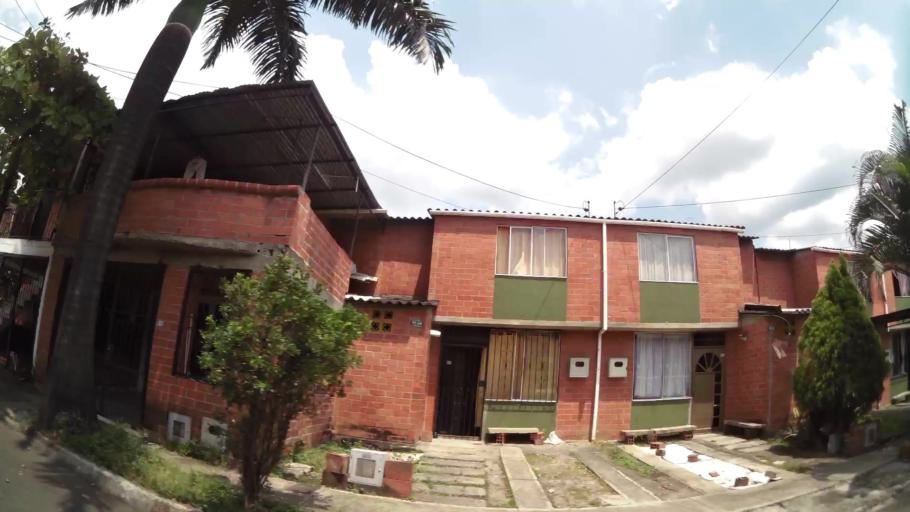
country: CO
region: Valle del Cauca
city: Cali
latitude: 3.4599
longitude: -76.4657
